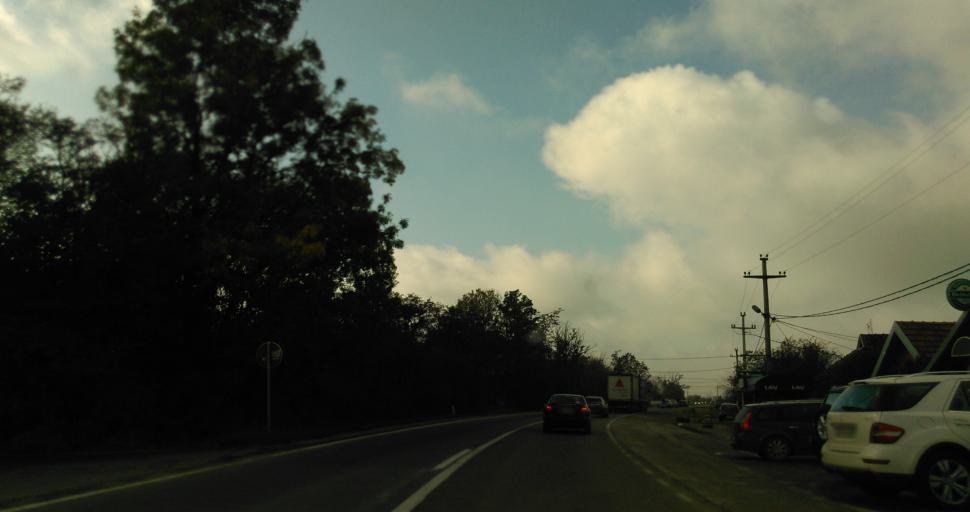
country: RS
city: Stepojevac
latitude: 44.5310
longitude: 20.2969
